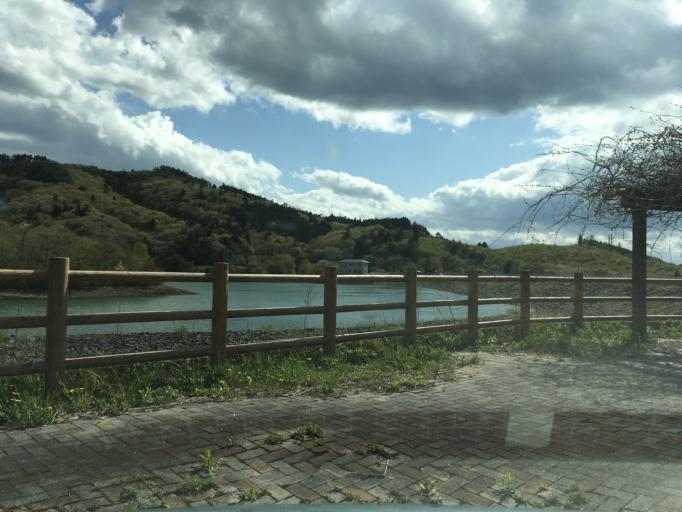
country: JP
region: Iwate
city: Ichinoseki
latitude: 38.8445
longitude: 141.3963
